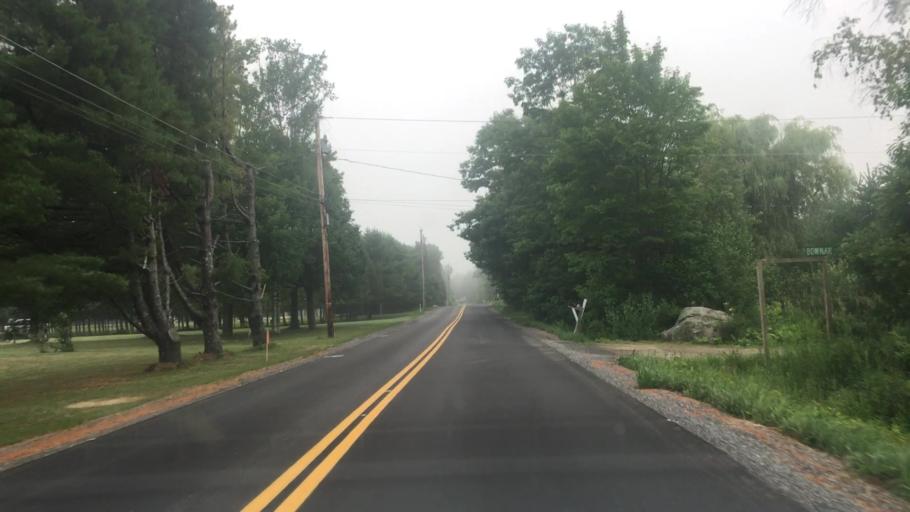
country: US
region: Maine
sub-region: Kennebec County
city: Oakland
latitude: 44.5172
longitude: -69.7221
